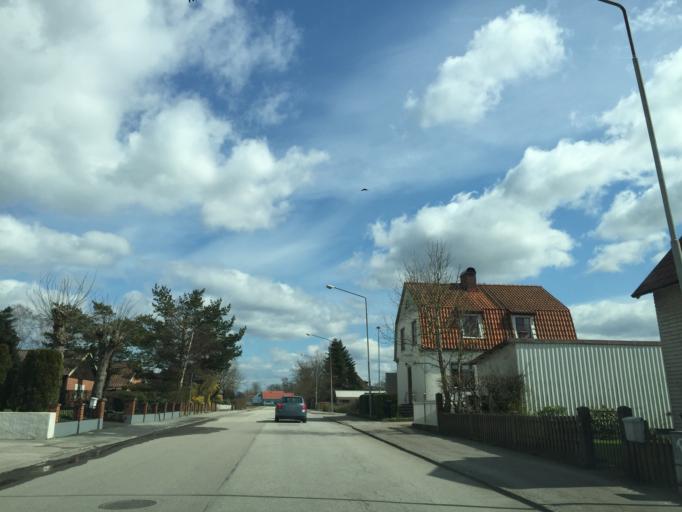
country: SE
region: Skane
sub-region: Horby Kommun
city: Hoerby
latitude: 55.8582
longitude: 13.6564
